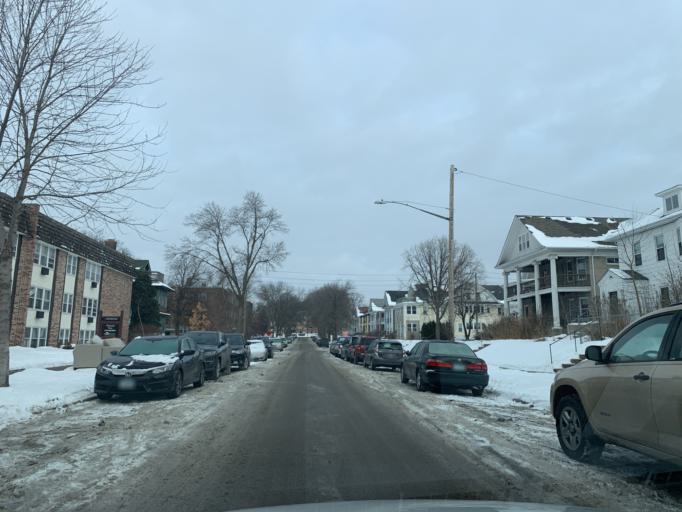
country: US
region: Minnesota
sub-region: Hennepin County
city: Minneapolis
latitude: 44.9601
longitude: -93.2829
